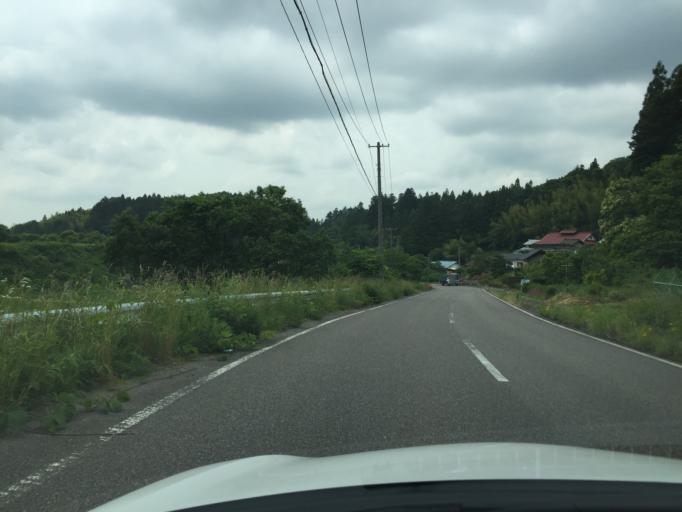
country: JP
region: Fukushima
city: Funehikimachi-funehiki
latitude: 37.3045
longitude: 140.5519
